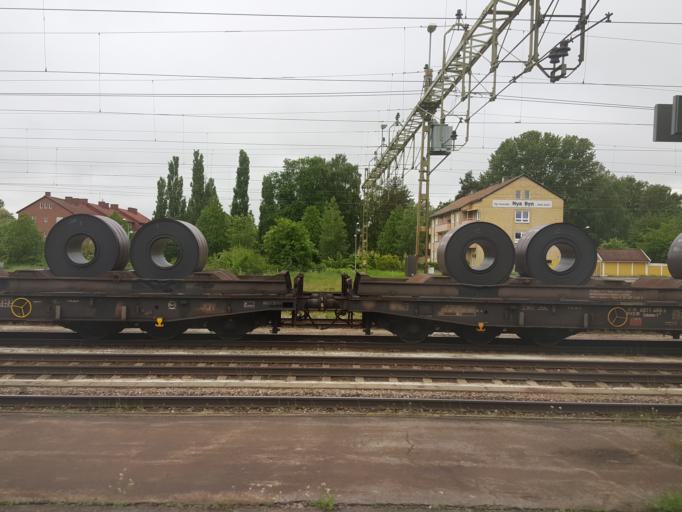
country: SE
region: Dalarna
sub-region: Avesta Kommun
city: Avesta
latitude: 60.1279
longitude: 16.2170
